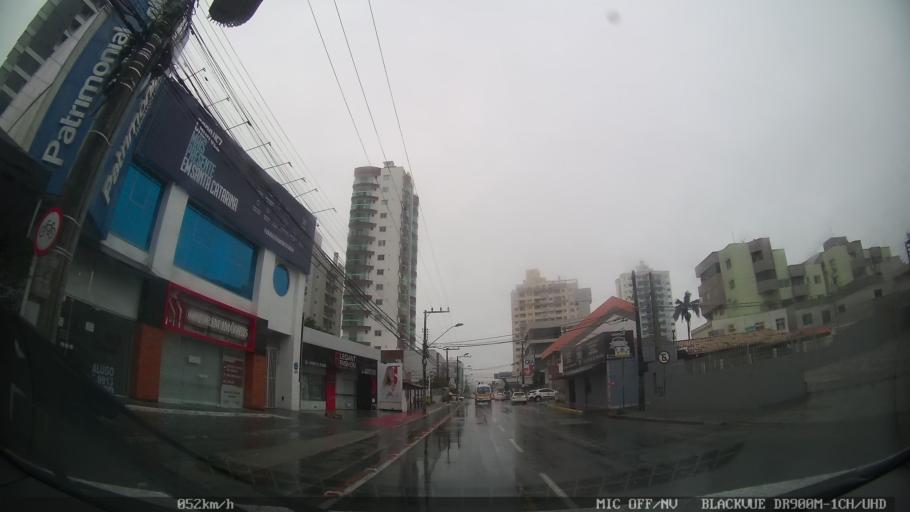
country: BR
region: Santa Catarina
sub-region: Itajai
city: Itajai
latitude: -26.9119
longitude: -48.6662
